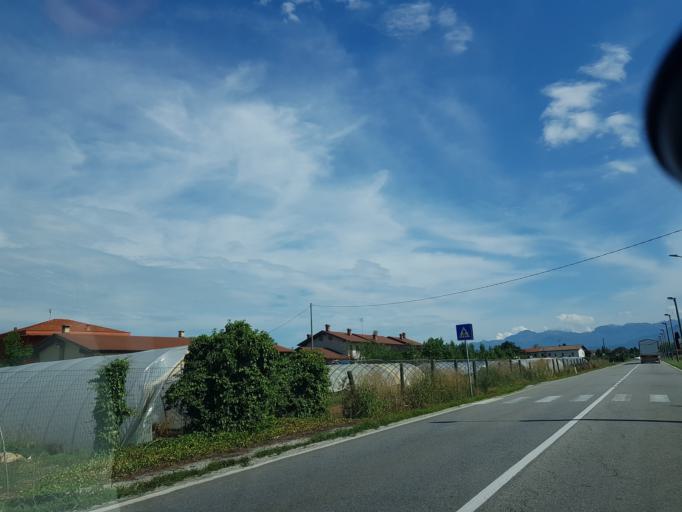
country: IT
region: Piedmont
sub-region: Provincia di Cuneo
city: Roata Rossi
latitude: 44.4431
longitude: 7.5305
